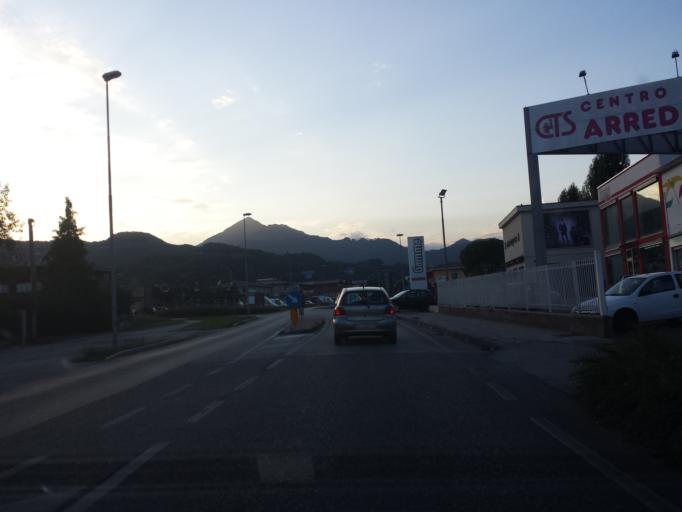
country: IT
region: Veneto
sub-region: Provincia di Vicenza
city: Cornedo Vicentino
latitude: 45.6199
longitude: 11.3214
